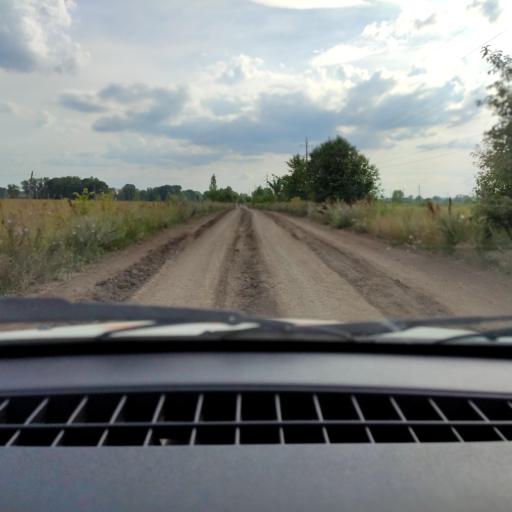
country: RU
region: Bashkortostan
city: Blagoveshchensk
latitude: 54.9258
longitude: 55.9454
